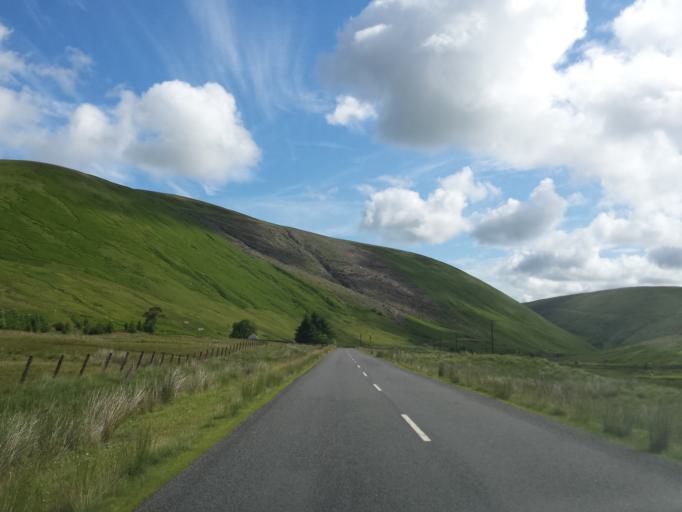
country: GB
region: Scotland
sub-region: Dumfries and Galloway
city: Moffat
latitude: 55.4374
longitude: -3.2557
